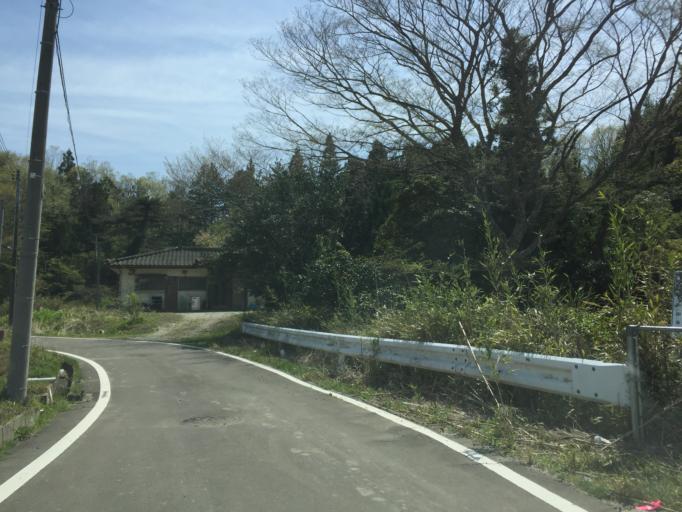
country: JP
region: Miyagi
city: Watari
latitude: 37.8977
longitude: 140.9266
